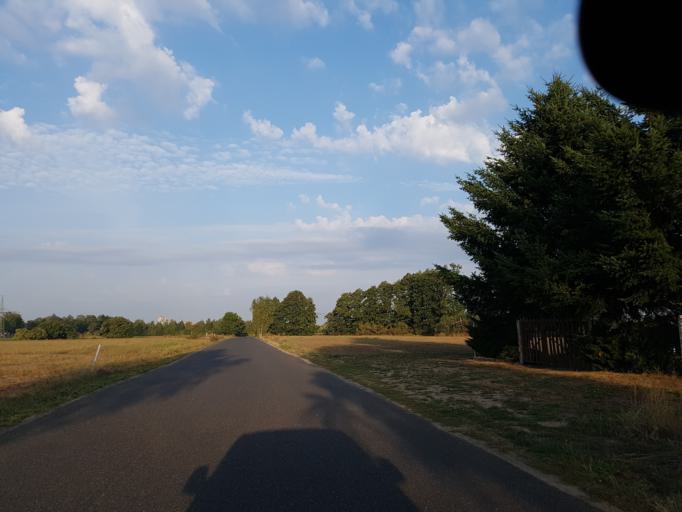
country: DE
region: Brandenburg
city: Elsterwerda
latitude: 51.4579
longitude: 13.5487
